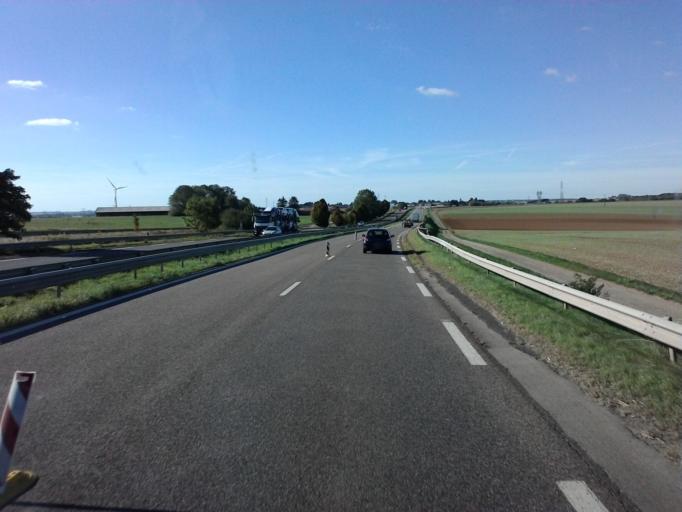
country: FR
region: Lorraine
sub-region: Departement de Meurthe-et-Moselle
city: Villers-la-Montagne
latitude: 49.4773
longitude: 5.8251
